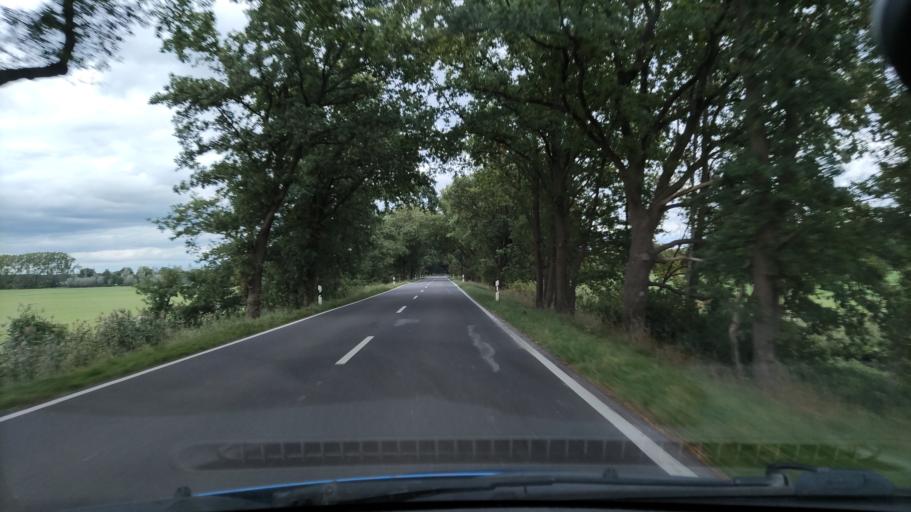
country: DE
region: Lower Saxony
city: Neu Darchau
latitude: 53.3428
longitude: 10.9536
